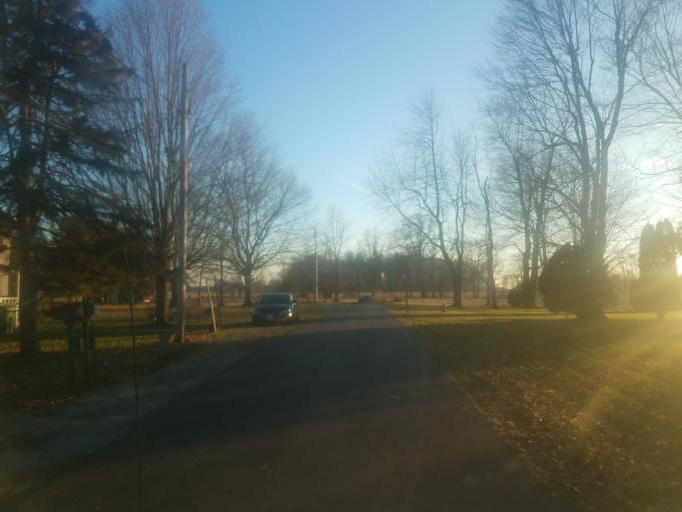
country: US
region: Ohio
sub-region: Wyandot County
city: Upper Sandusky
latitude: 40.8128
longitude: -83.1329
